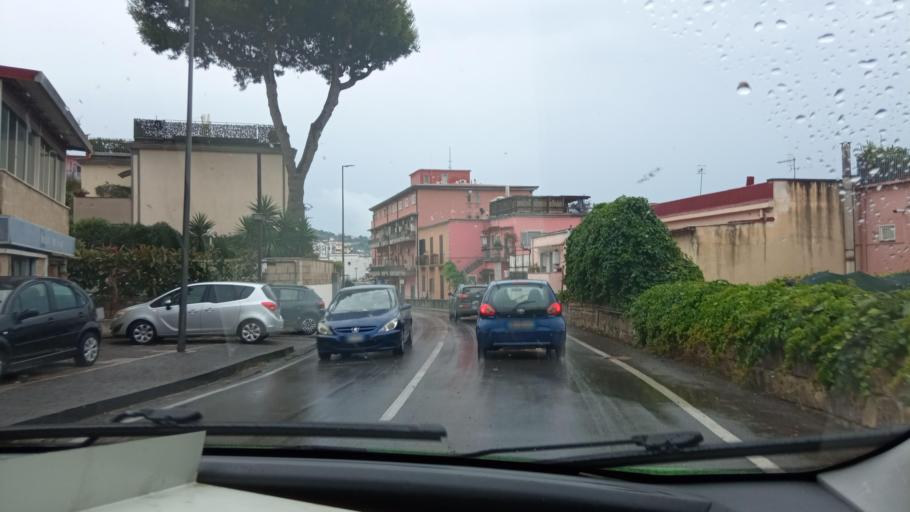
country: IT
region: Campania
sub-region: Provincia di Napoli
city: Pozzuoli
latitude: 40.8315
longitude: 14.1173
